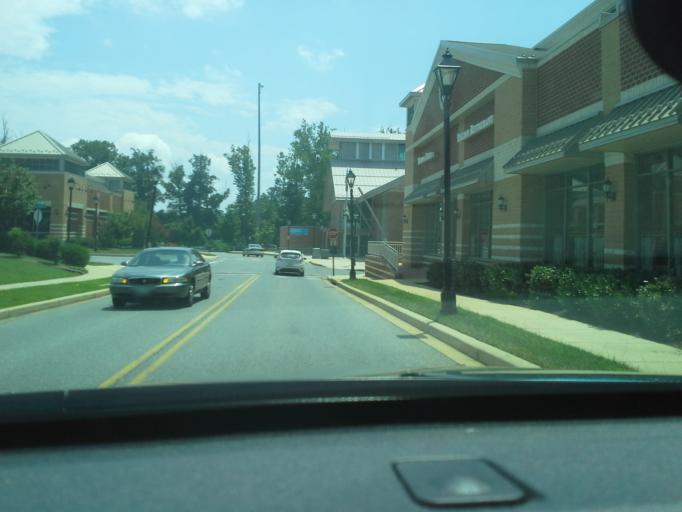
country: US
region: Maryland
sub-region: Calvert County
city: Prince Frederick
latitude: 38.5569
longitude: -76.5994
